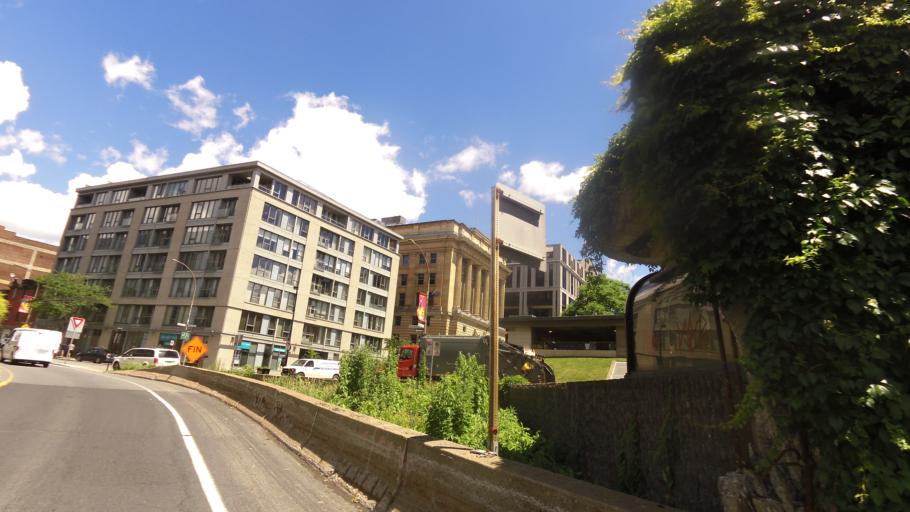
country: CA
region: Quebec
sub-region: Montreal
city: Montreal
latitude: 45.5097
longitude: -73.5556
